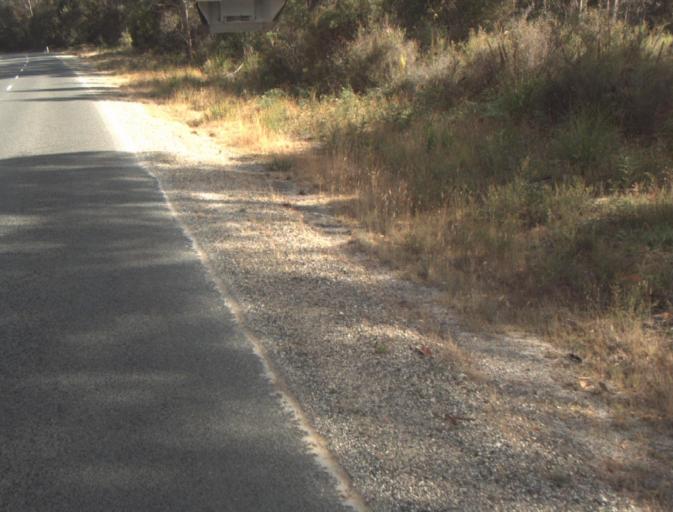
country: AU
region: Tasmania
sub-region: Dorset
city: Bridport
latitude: -41.1278
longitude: 147.2121
